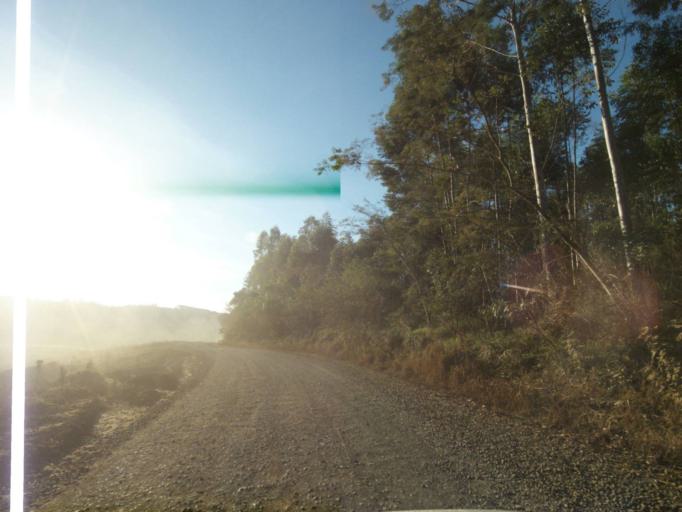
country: BR
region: Parana
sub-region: Telemaco Borba
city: Telemaco Borba
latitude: -24.4214
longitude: -50.5893
